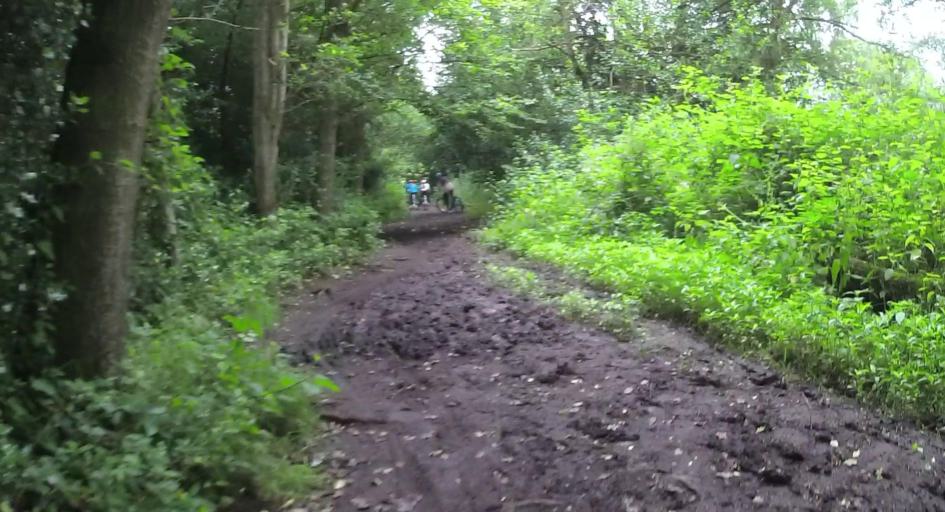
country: GB
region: England
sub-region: Wokingham
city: Finchampstead
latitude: 51.3589
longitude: -0.8656
